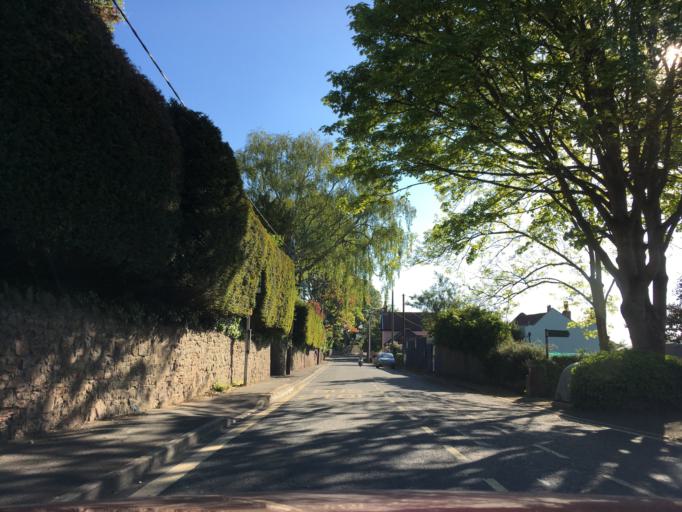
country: GB
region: England
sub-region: North Somerset
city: Long Ashton
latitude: 51.4308
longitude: -2.6560
